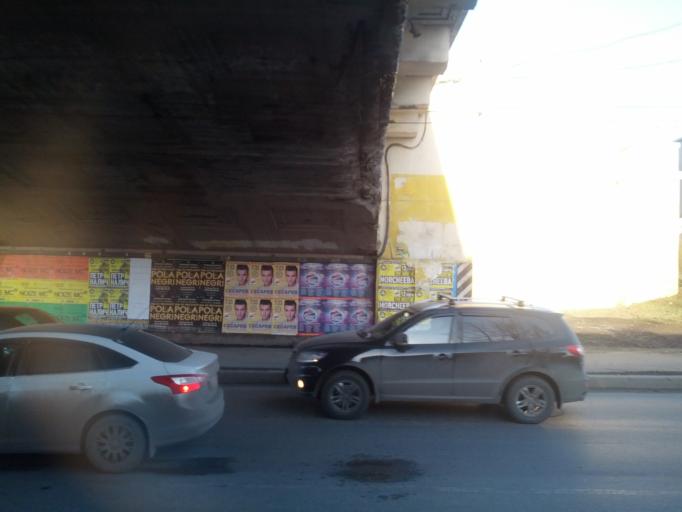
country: RU
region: St.-Petersburg
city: Centralniy
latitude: 59.9194
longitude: 30.4236
